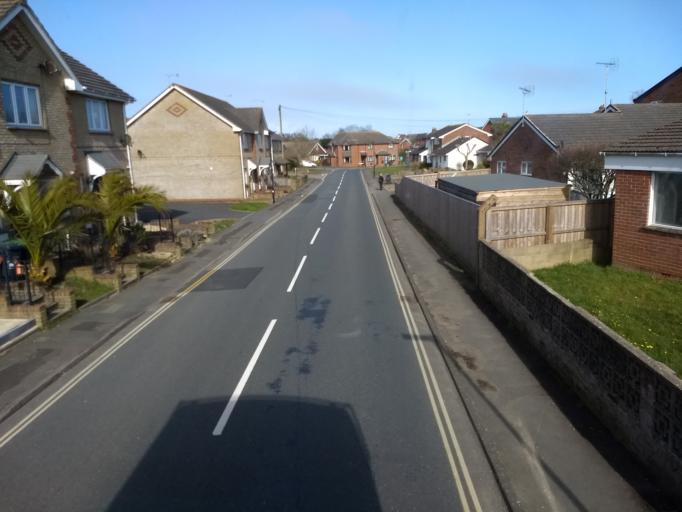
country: GB
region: England
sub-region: Isle of Wight
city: Sandown
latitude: 50.6425
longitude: -1.1712
